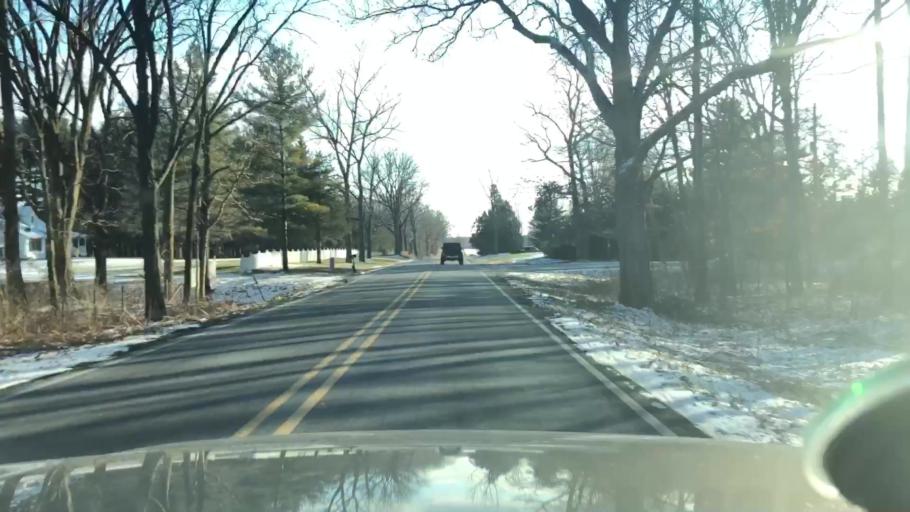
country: US
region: Michigan
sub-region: Jackson County
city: Vandercook Lake
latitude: 42.1056
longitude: -84.4512
